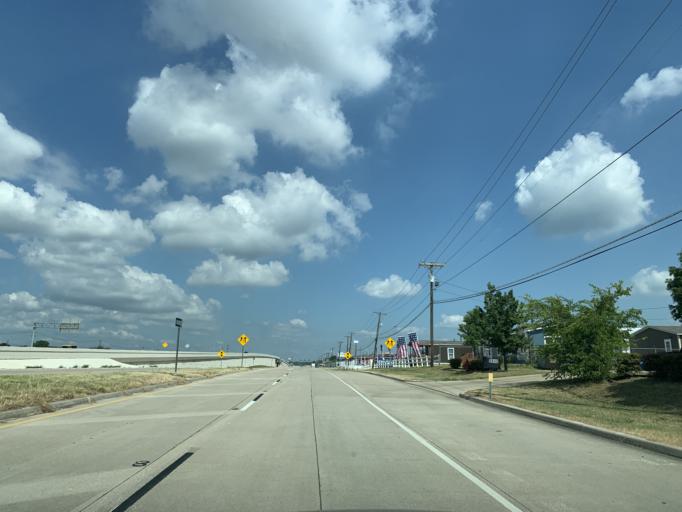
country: US
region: Texas
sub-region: Tarrant County
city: Lakeside
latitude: 32.8352
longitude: -97.4882
